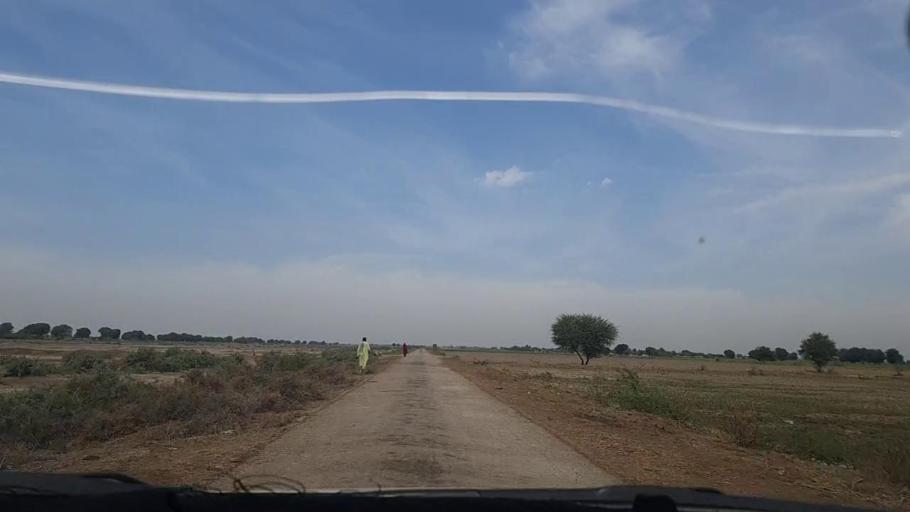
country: PK
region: Sindh
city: Pithoro
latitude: 25.4620
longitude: 69.4700
